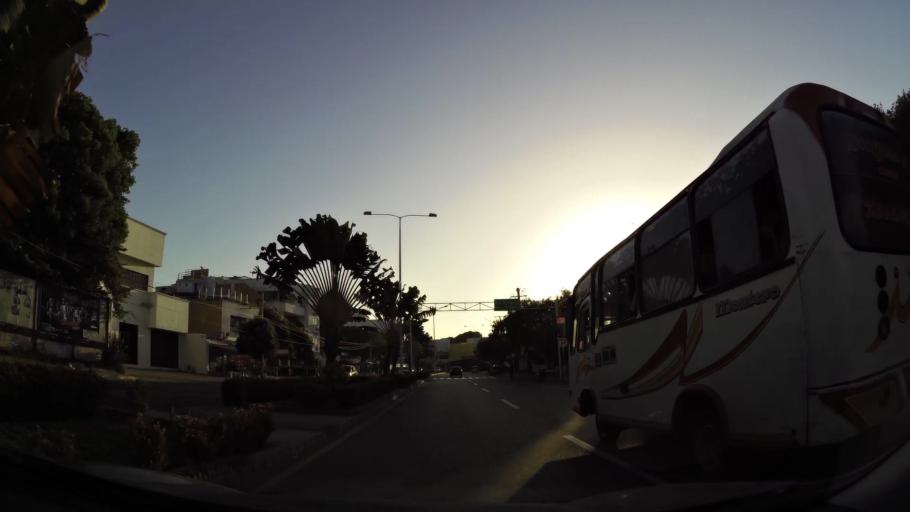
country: CO
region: Bolivar
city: Cartagena
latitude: 10.4427
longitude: -75.5192
